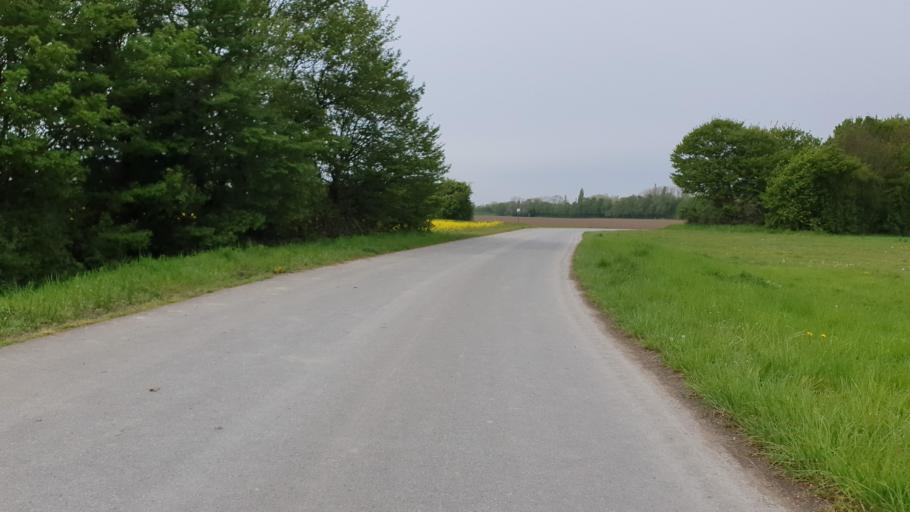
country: DE
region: North Rhine-Westphalia
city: Monheim am Rhein
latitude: 51.0810
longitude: 6.8787
